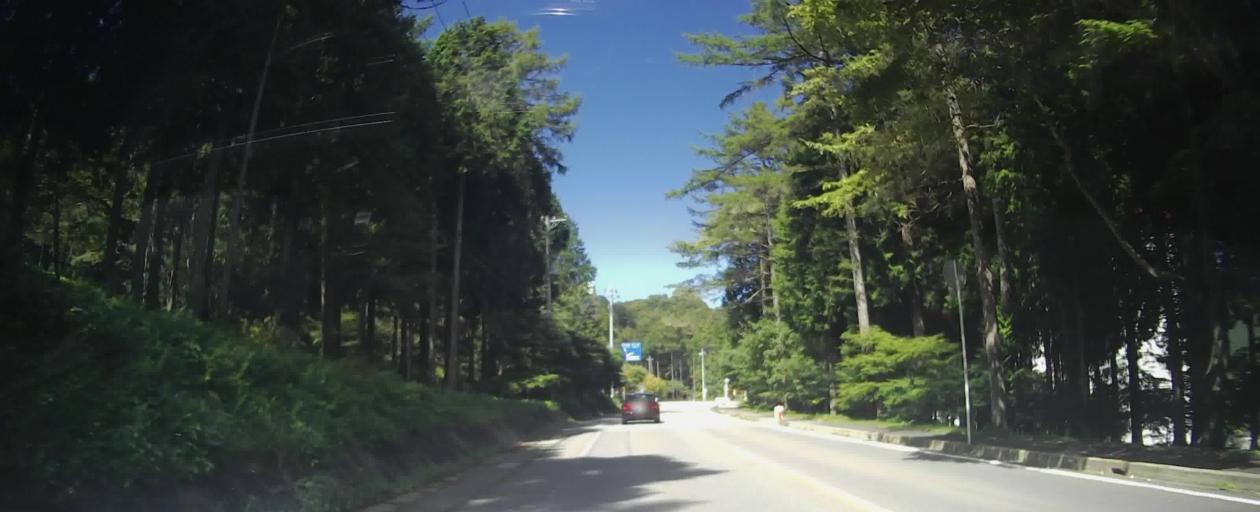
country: JP
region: Gunma
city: Nakanojomachi
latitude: 36.4760
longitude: 138.8608
